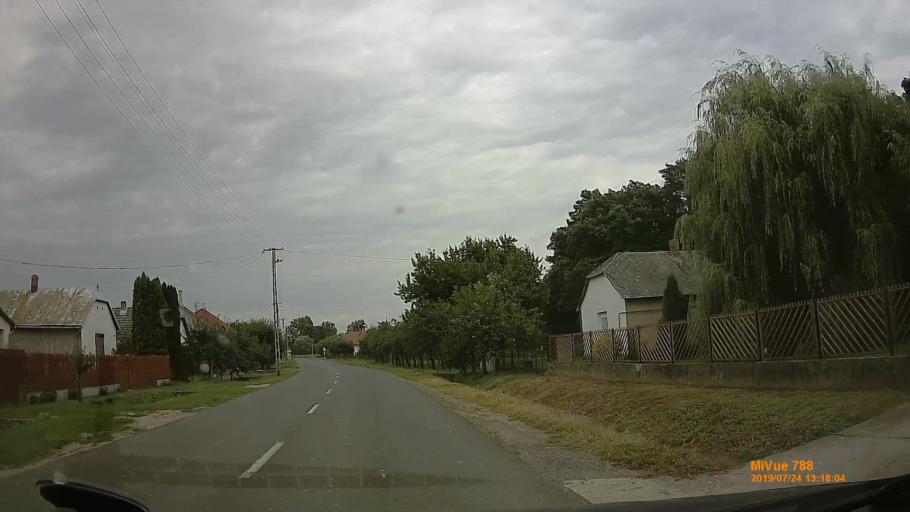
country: HU
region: Szabolcs-Szatmar-Bereg
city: Vasarosnameny
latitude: 48.1918
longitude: 22.3978
